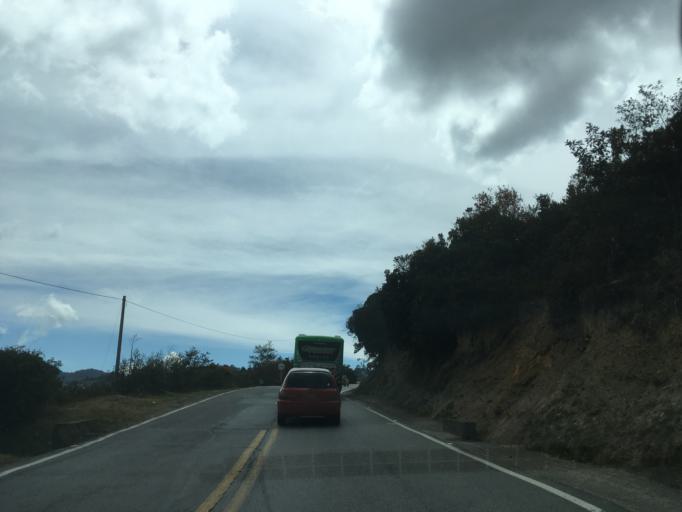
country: CO
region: Boyaca
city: Sogamoso
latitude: 5.6380
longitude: -72.9183
